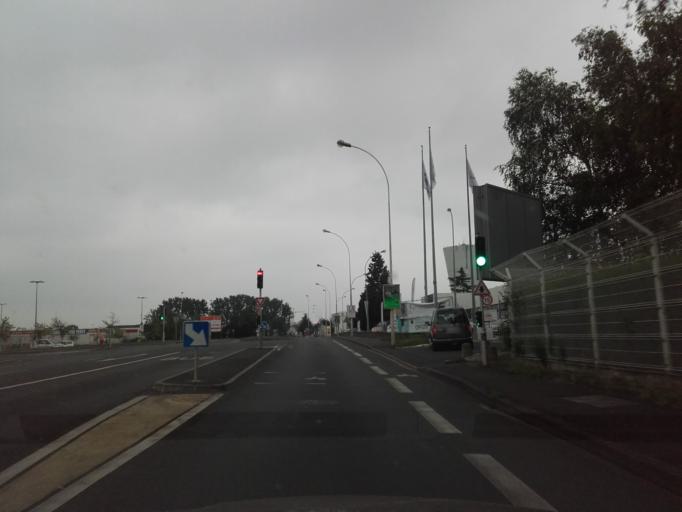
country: FR
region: Centre
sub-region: Departement d'Indre-et-Loire
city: Saint-Cyr-sur-Loire
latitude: 47.4272
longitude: 0.6967
